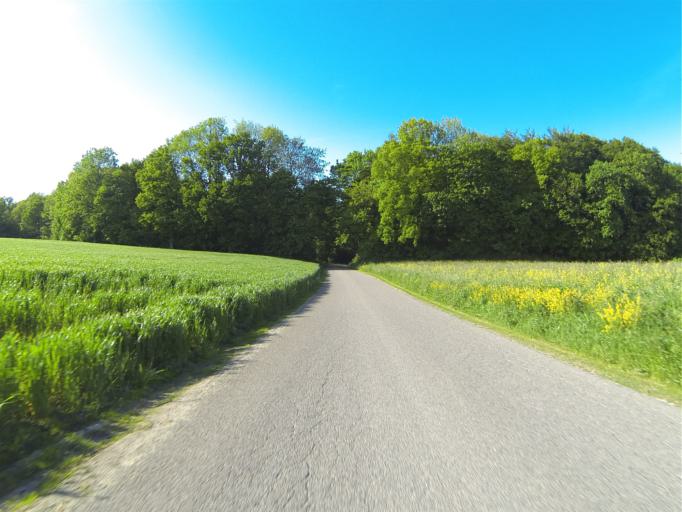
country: SE
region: Skane
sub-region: Lunds Kommun
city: Genarp
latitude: 55.7064
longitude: 13.3693
